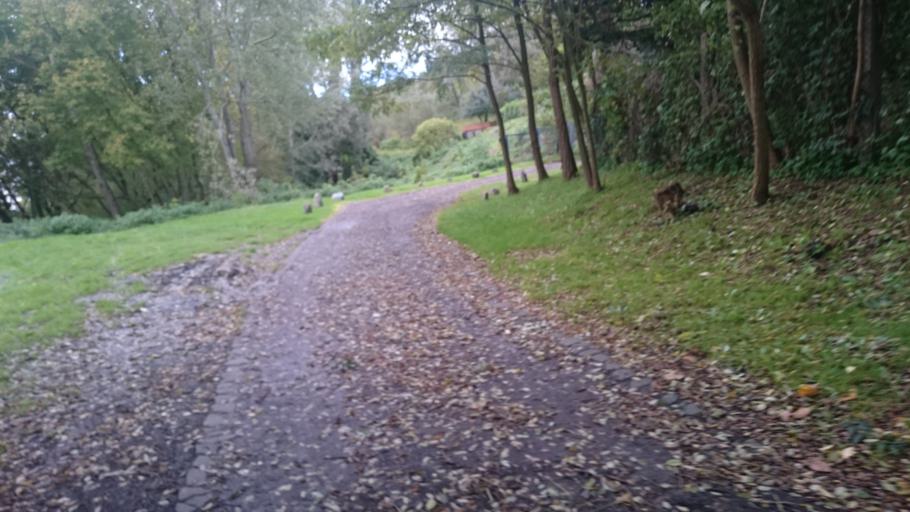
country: PL
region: Kujawsko-Pomorskie
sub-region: Grudziadz
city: Grudziadz
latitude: 53.5020
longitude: 18.7515
